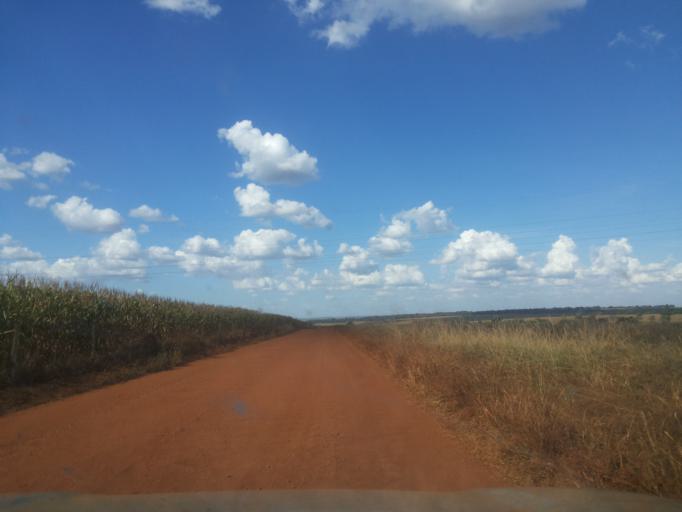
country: BR
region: Minas Gerais
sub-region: Capinopolis
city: Capinopolis
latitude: -18.5823
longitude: -49.5071
